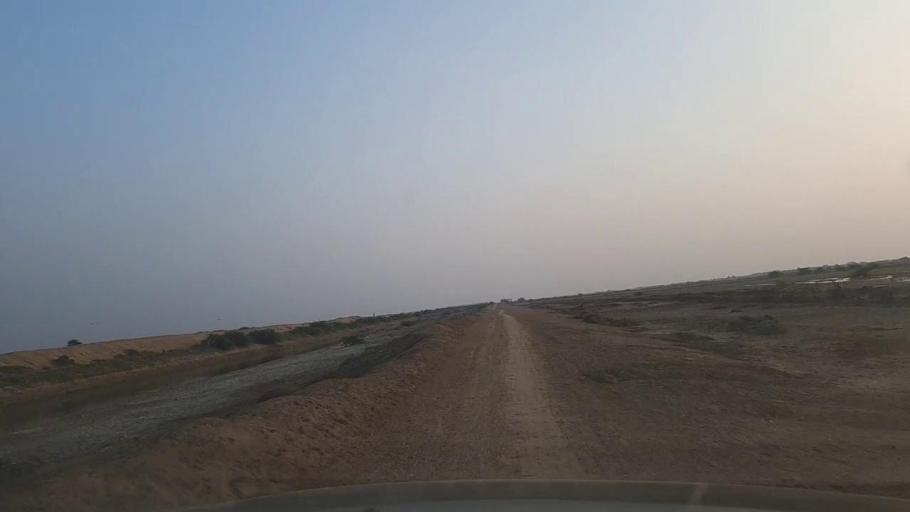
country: PK
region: Sindh
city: Jati
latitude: 24.5358
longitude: 68.4086
